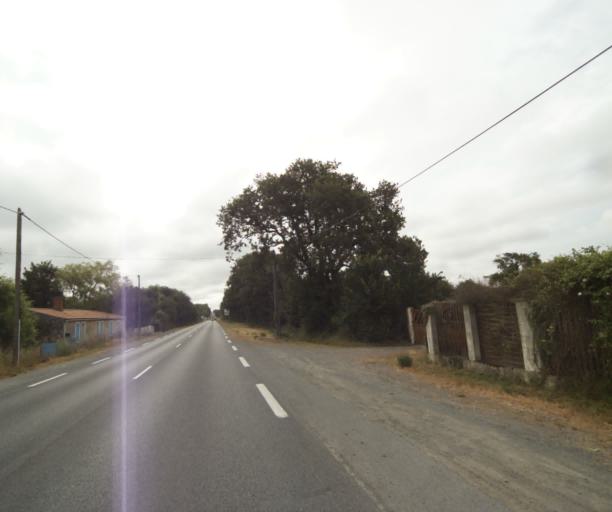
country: FR
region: Pays de la Loire
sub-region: Departement de la Vendee
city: Chateau-d'Olonne
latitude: 46.4808
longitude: -1.7093
